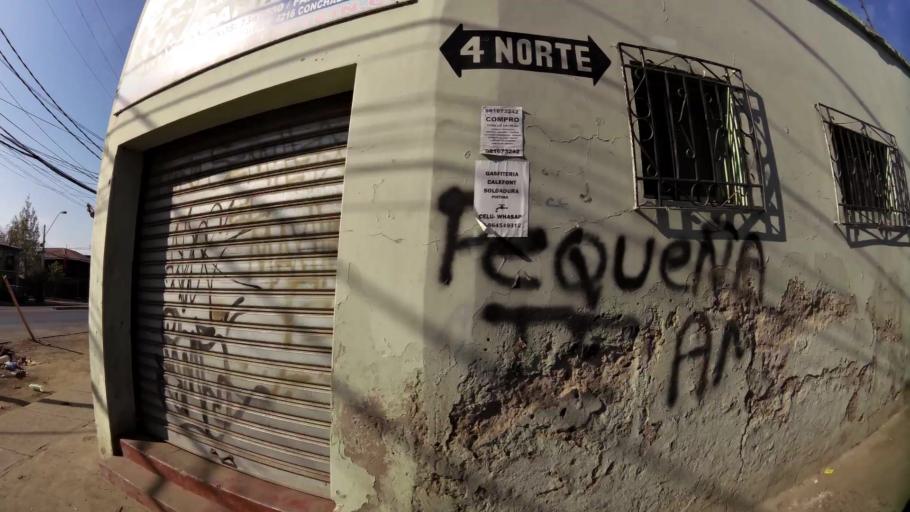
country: CL
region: Santiago Metropolitan
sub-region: Provincia de Santiago
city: Lo Prado
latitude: -33.3913
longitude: -70.6835
